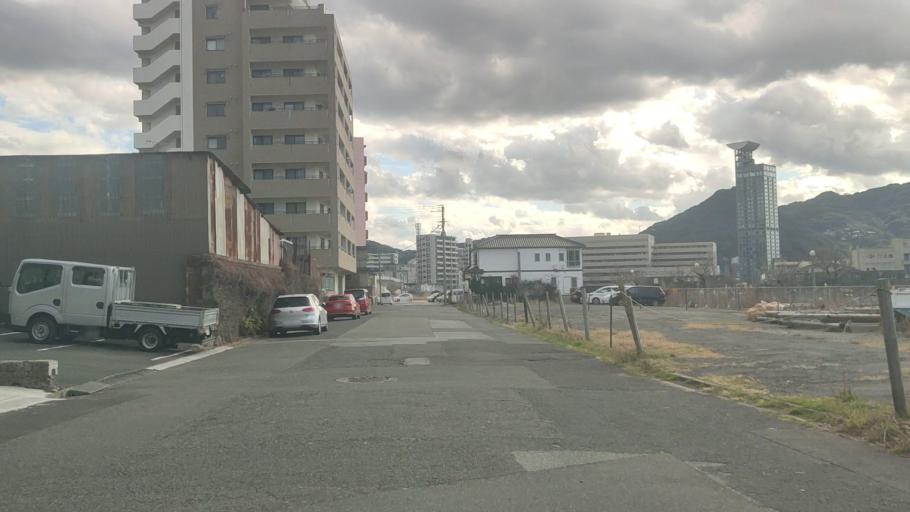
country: JP
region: Yamaguchi
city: Shimonoseki
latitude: 33.9556
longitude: 130.9647
